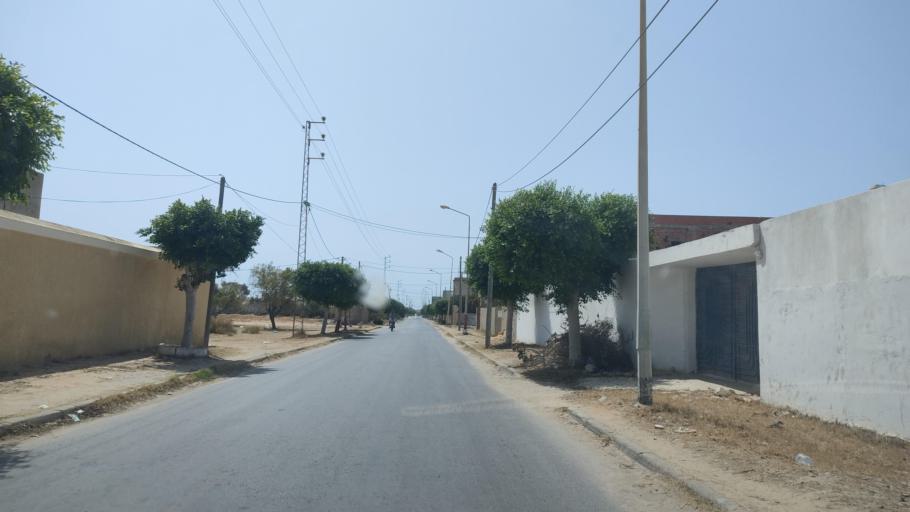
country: TN
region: Safaqis
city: Sfax
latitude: 34.6747
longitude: 10.7009
